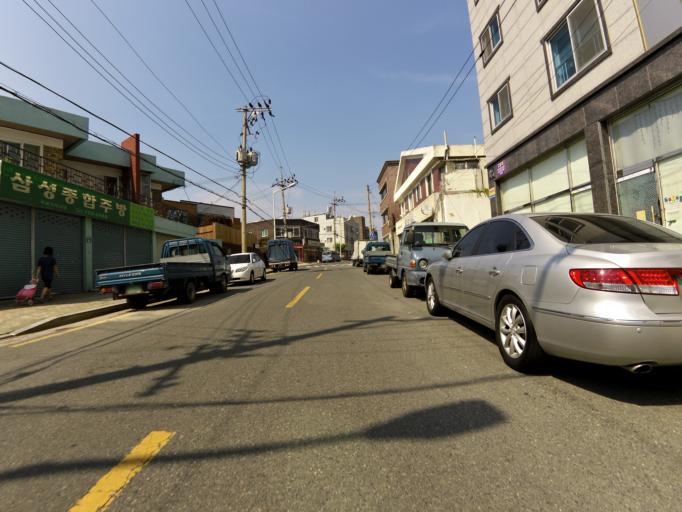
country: KR
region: Daegu
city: Daegu
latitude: 35.8708
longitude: 128.6428
